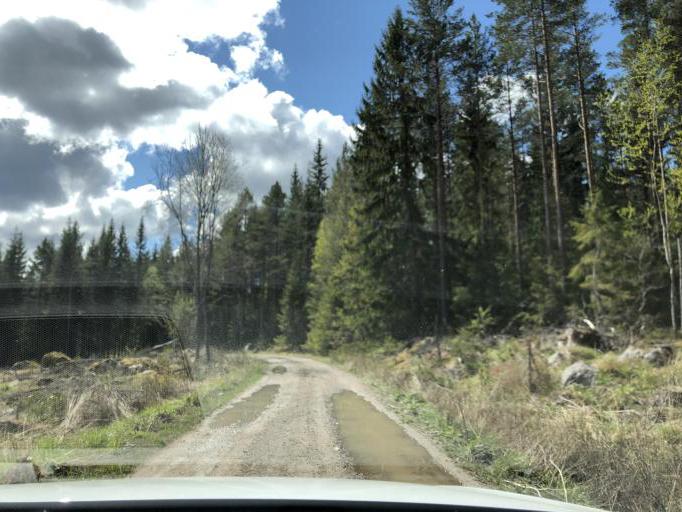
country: SE
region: Uppsala
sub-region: Heby Kommun
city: Tarnsjo
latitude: 60.2360
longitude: 16.7091
